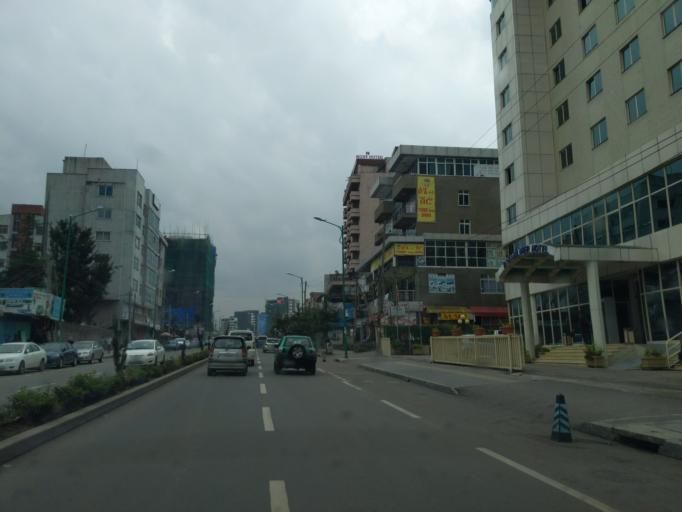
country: ET
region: Adis Abeba
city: Addis Ababa
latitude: 8.9949
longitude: 38.7667
